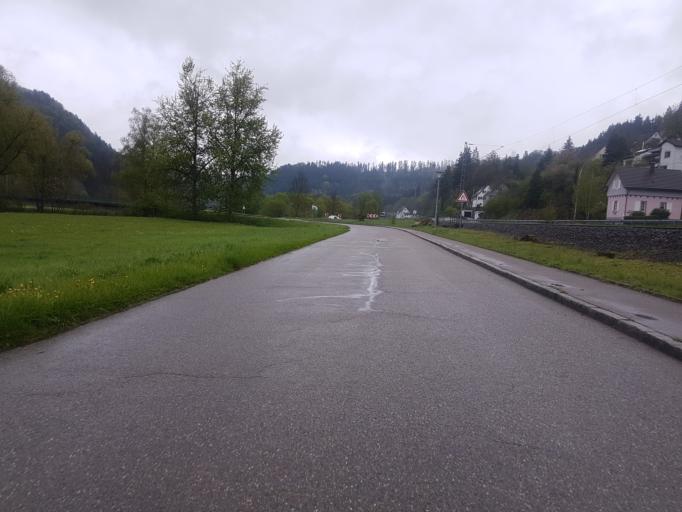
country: DE
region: Baden-Wuerttemberg
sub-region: Freiburg Region
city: Epfendorf
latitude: 48.2436
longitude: 8.5998
